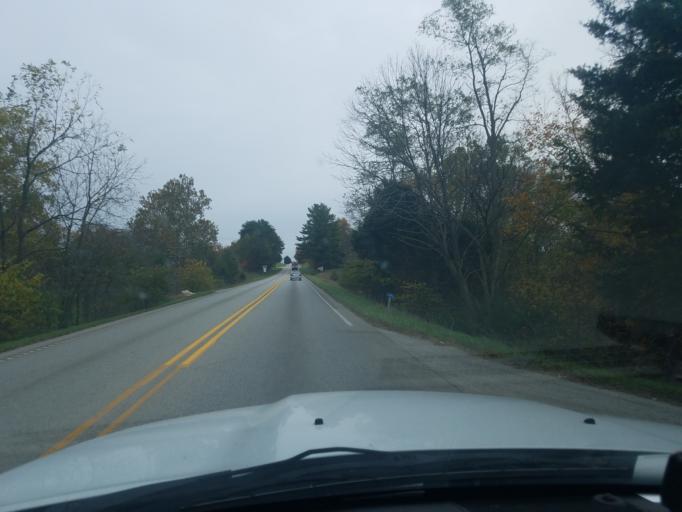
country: US
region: Indiana
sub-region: Washington County
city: Salem
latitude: 38.5851
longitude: -86.0646
